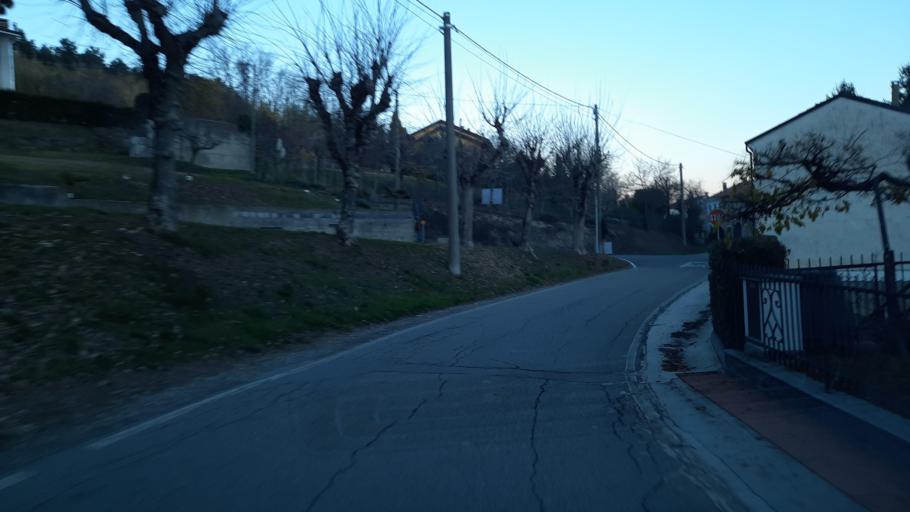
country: IT
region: Piedmont
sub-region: Provincia di Alessandria
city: Camino
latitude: 45.1619
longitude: 8.2838
